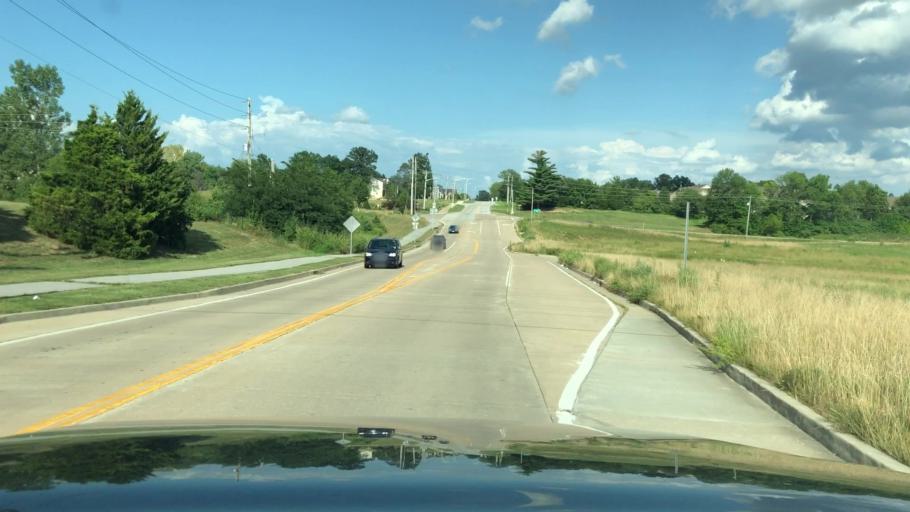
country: US
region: Missouri
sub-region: Saint Charles County
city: Lake Saint Louis
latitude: 38.7959
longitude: -90.8176
